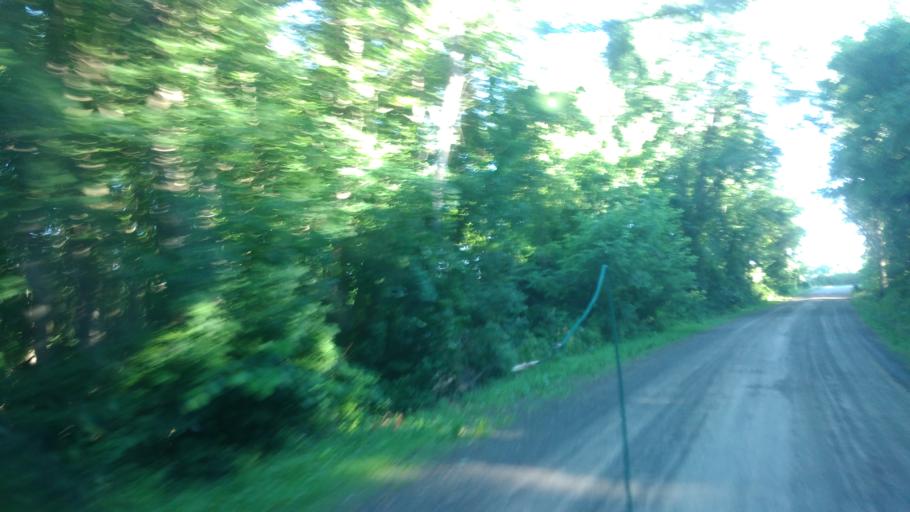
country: US
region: New York
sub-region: Wayne County
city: Sodus
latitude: 43.1644
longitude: -77.0586
